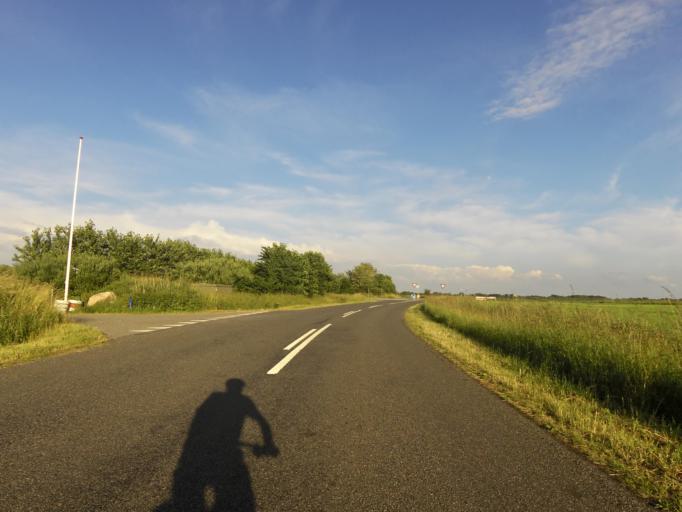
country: DK
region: South Denmark
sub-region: Tonder Kommune
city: Sherrebek
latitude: 55.1672
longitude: 8.7463
